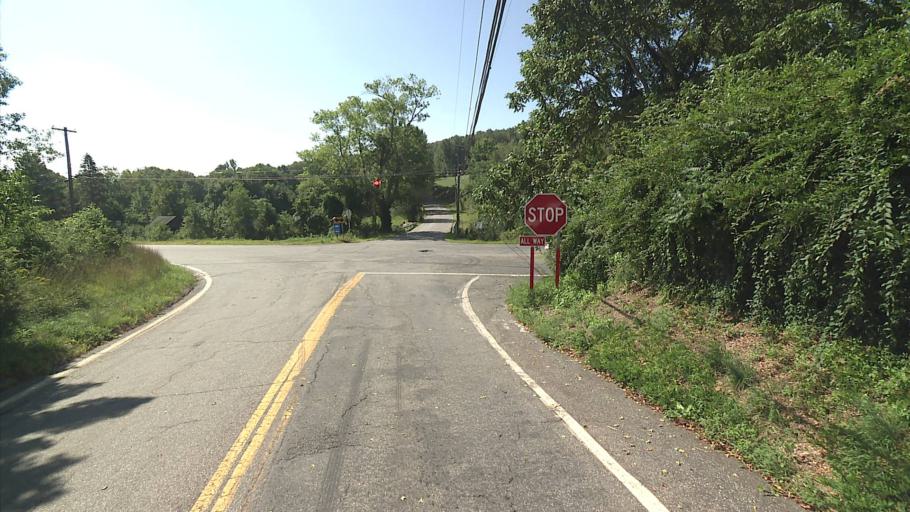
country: US
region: Connecticut
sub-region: Tolland County
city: Stafford Springs
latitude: 41.9177
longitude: -72.1918
